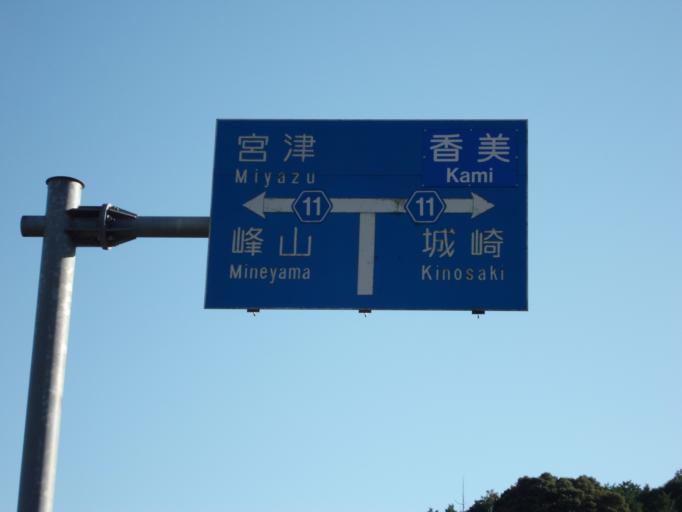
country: JP
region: Hyogo
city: Toyooka
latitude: 35.6131
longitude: 134.8889
